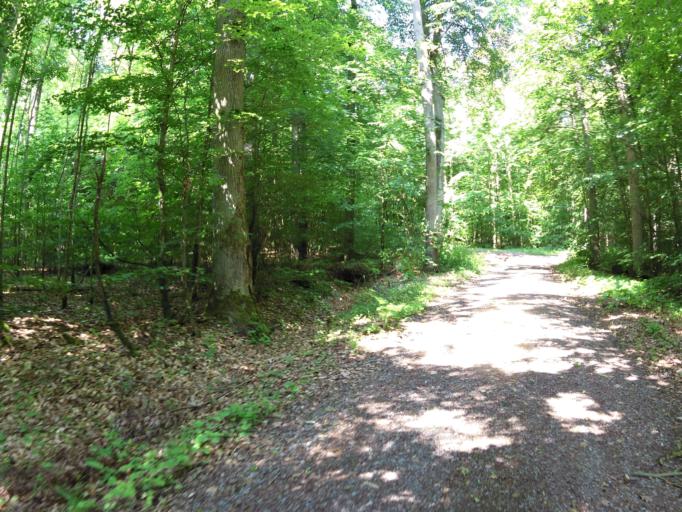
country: DE
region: Bavaria
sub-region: Regierungsbezirk Unterfranken
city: Wuerzburg
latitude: 49.7299
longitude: 9.8774
